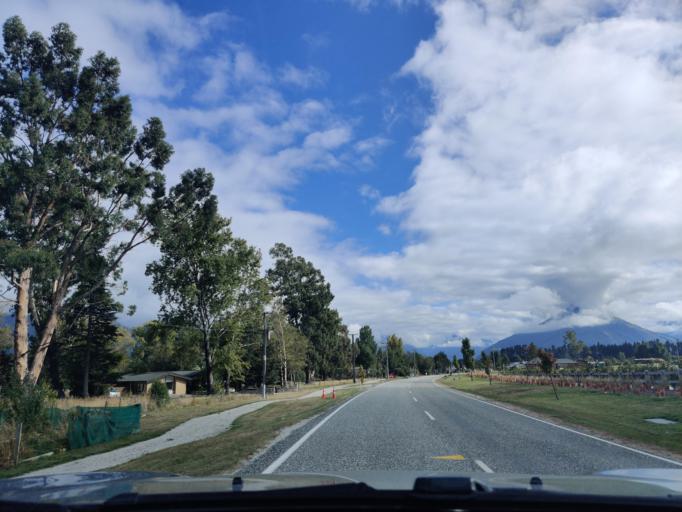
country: NZ
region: Otago
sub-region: Queenstown-Lakes District
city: Queenstown
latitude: -44.8565
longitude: 168.3913
